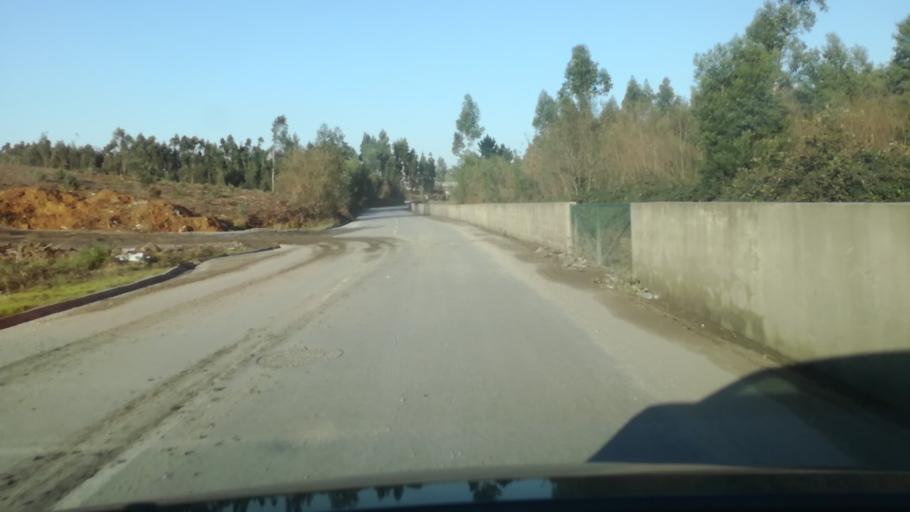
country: PT
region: Braga
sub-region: Vila Nova de Famalicao
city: Ferreiros
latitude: 41.3619
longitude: -8.5366
